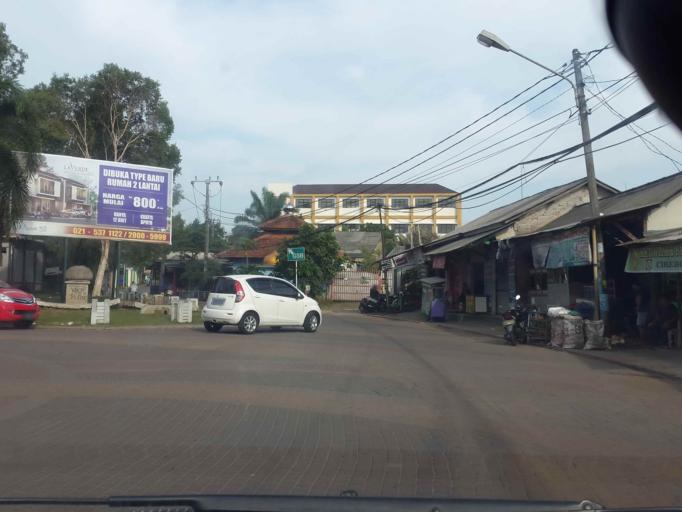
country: ID
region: West Java
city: Serpong
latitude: -6.2793
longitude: 106.6695
